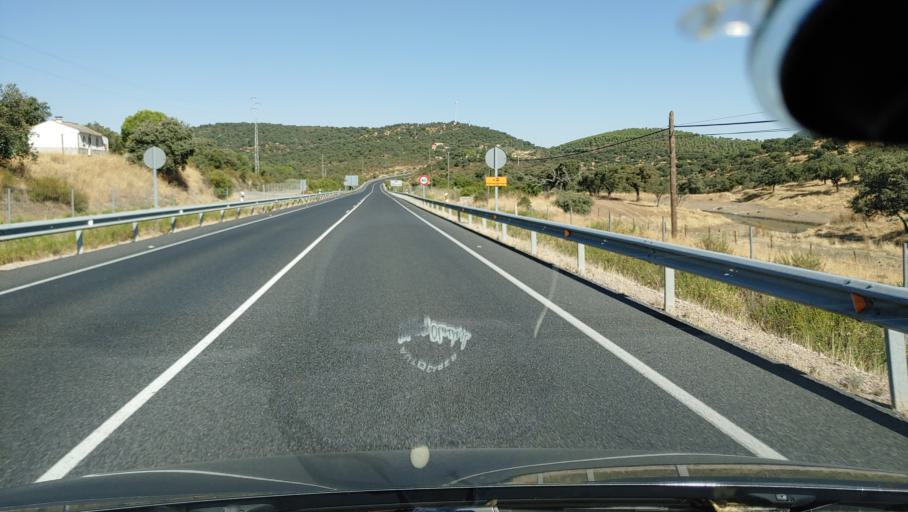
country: ES
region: Andalusia
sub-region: Province of Cordoba
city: Villaharta
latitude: 38.0998
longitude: -4.8744
